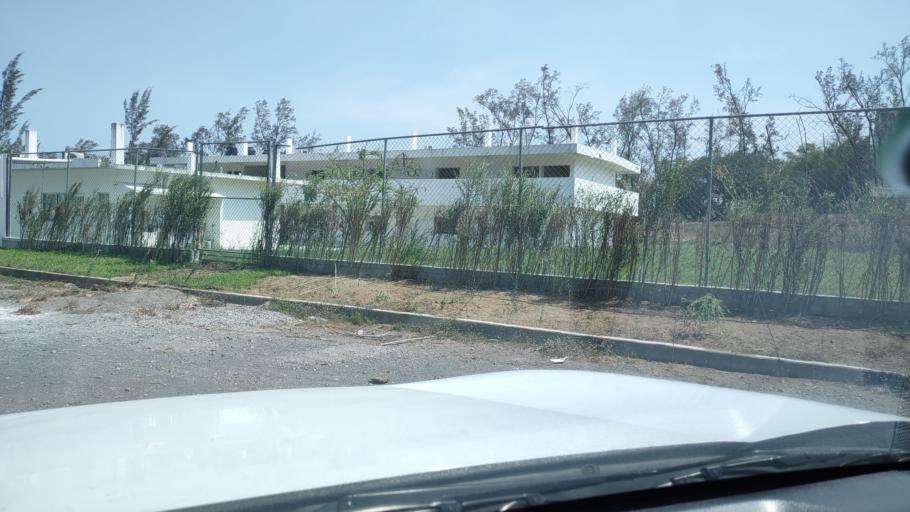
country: MX
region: Veracruz
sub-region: Veracruz
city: Las Amapolas
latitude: 19.1497
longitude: -96.2243
